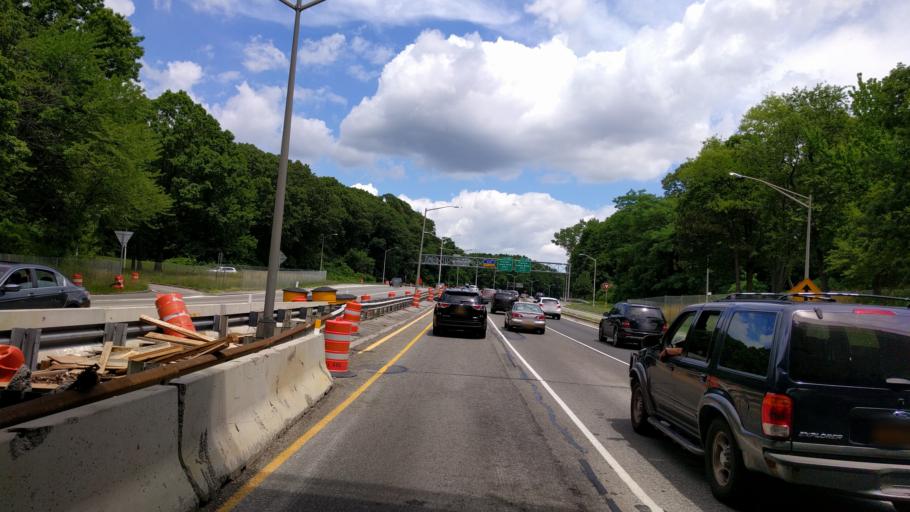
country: US
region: New York
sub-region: Queens County
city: Jamaica
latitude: 40.7223
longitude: -73.7773
